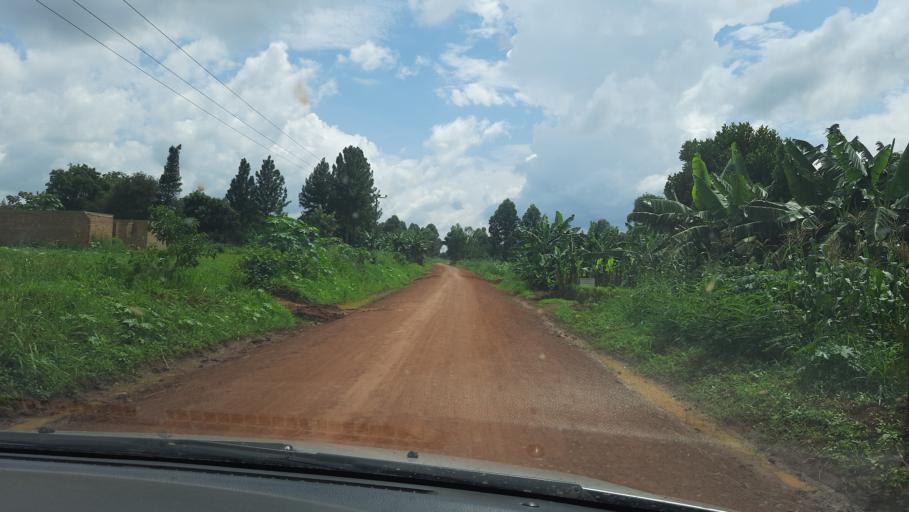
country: UG
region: Western Region
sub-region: Kiryandongo District
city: Kiryandongo
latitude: 1.8125
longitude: 31.9979
